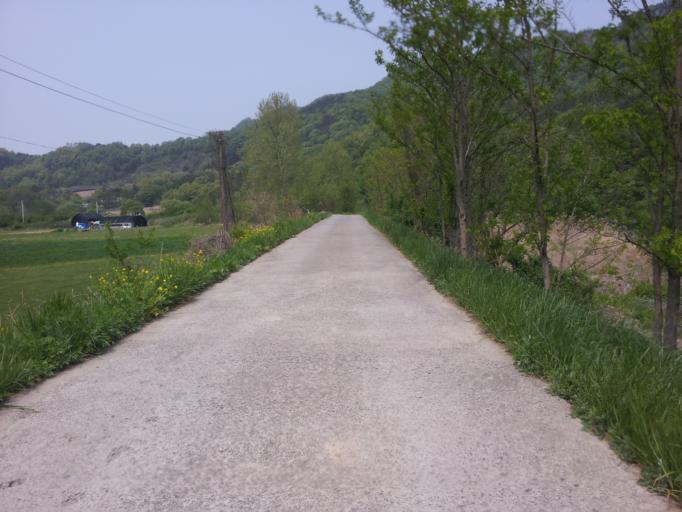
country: KR
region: Daejeon
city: Daejeon
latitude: 36.2796
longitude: 127.3371
